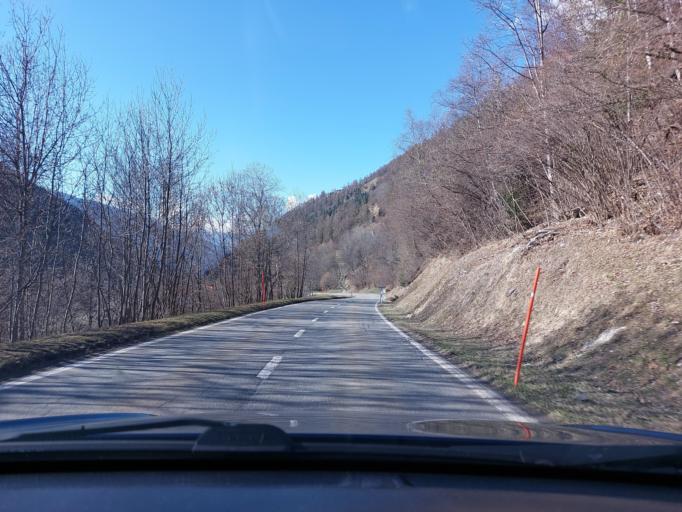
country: CH
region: Valais
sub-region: Herens District
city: Evolene
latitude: 46.1397
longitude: 7.4686
